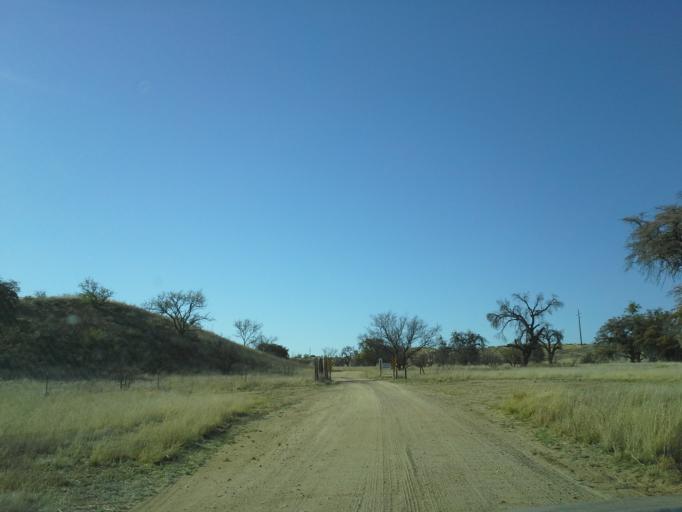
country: US
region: Arizona
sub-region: Pima County
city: Corona de Tucson
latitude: 31.7426
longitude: -110.6890
